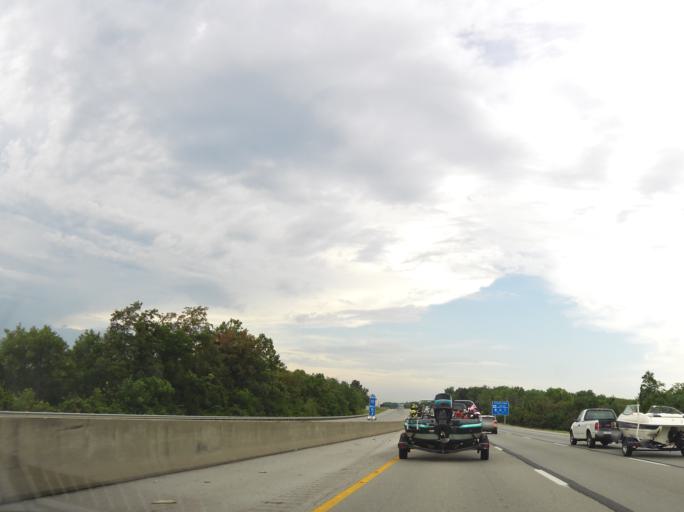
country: US
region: Kentucky
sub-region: Madison County
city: Berea
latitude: 37.5808
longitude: -84.3131
